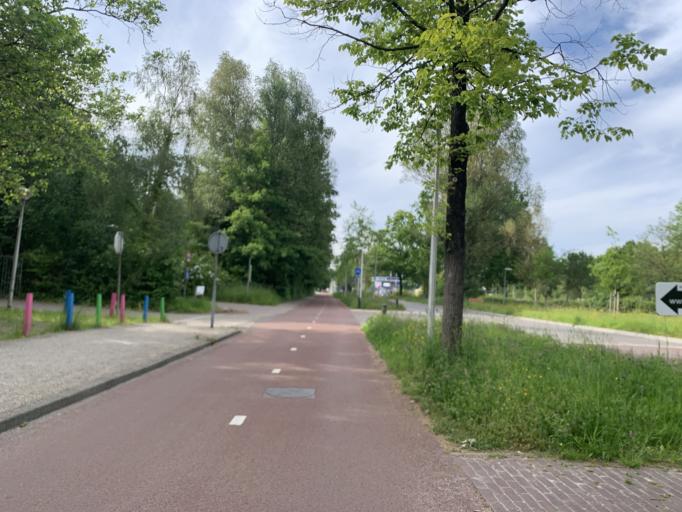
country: NL
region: Groningen
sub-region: Gemeente Haren
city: Haren
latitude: 53.1783
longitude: 6.6050
